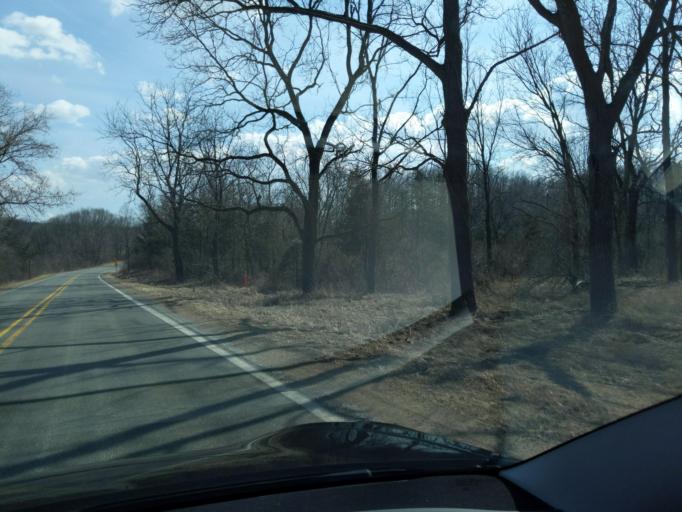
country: US
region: Michigan
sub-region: Washtenaw County
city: Chelsea
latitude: 42.4140
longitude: -84.0489
